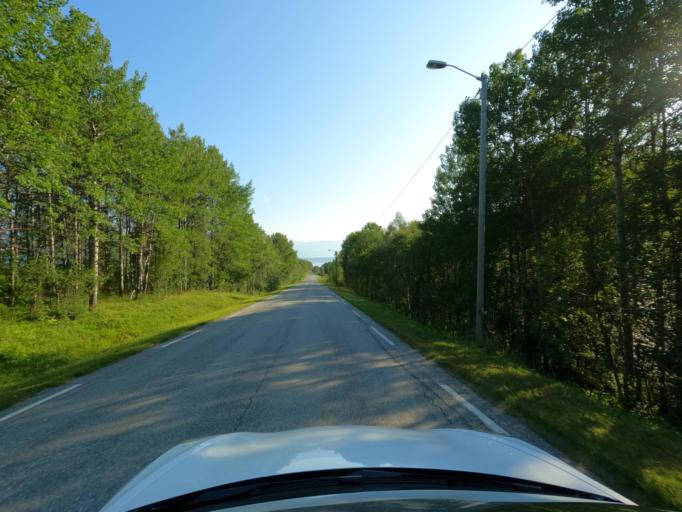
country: NO
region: Nordland
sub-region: Narvik
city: Bjerkvik
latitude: 68.5387
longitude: 17.4873
